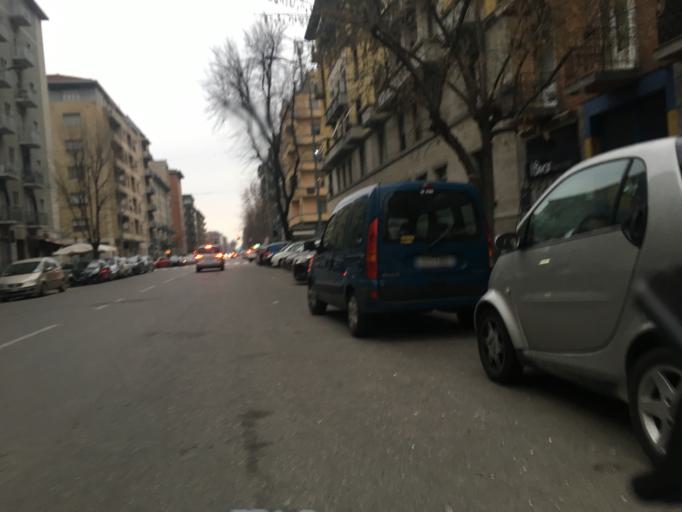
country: IT
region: Lombardy
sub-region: Citta metropolitana di Milano
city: Romano Banco
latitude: 45.4524
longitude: 9.1503
